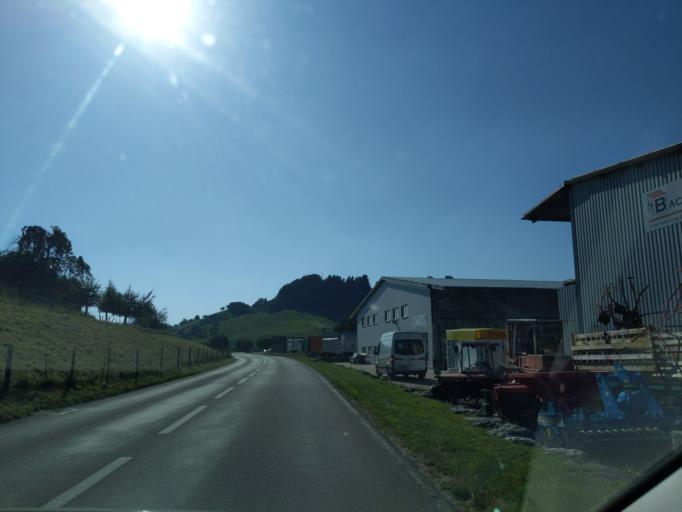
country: CH
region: Bern
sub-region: Oberaargau
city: Huttwil
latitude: 47.1278
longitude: 7.8873
